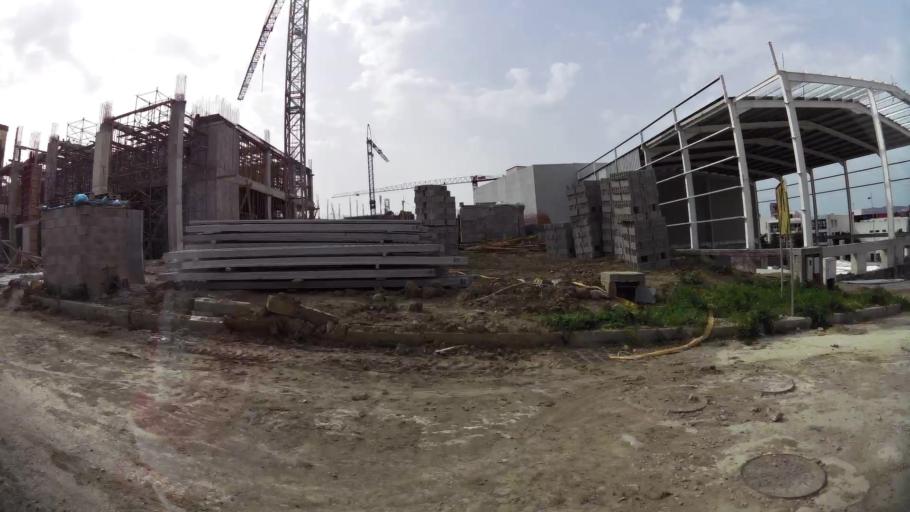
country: MA
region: Tanger-Tetouan
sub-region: Tanger-Assilah
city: Boukhalef
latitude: 35.7137
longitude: -5.9071
